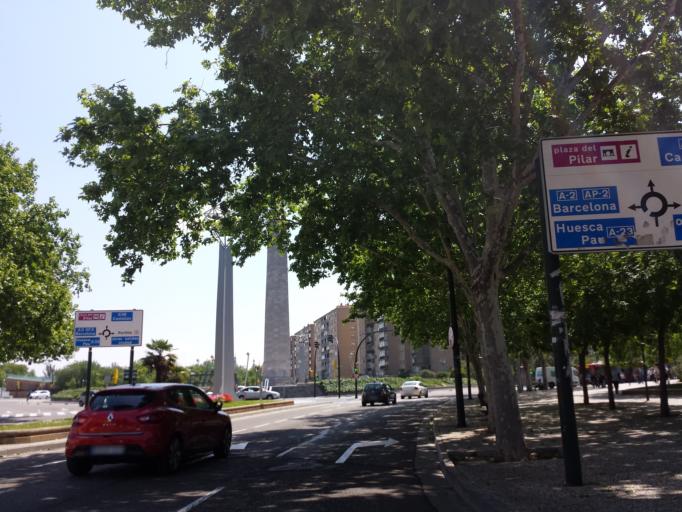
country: ES
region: Aragon
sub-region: Provincia de Zaragoza
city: Almozara
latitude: 41.6594
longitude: -0.8937
